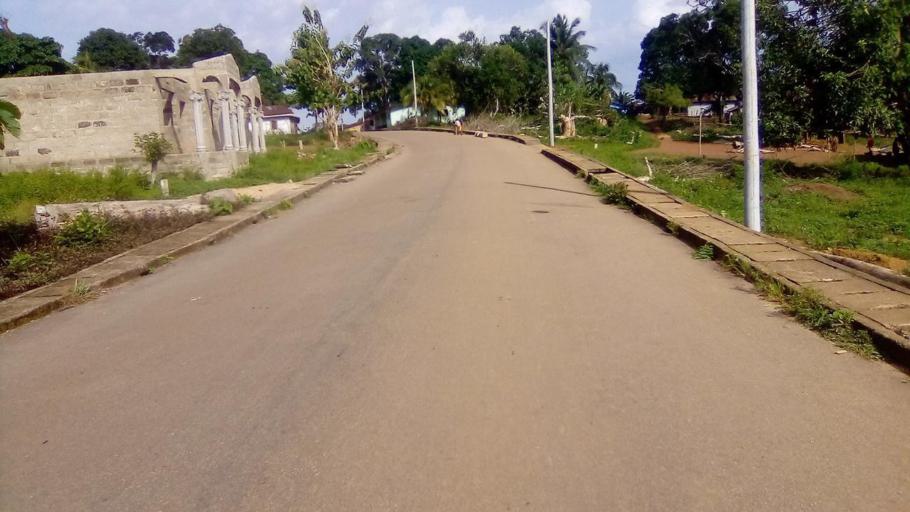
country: SL
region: Southern Province
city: Pujehun
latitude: 7.3581
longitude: -11.7161
